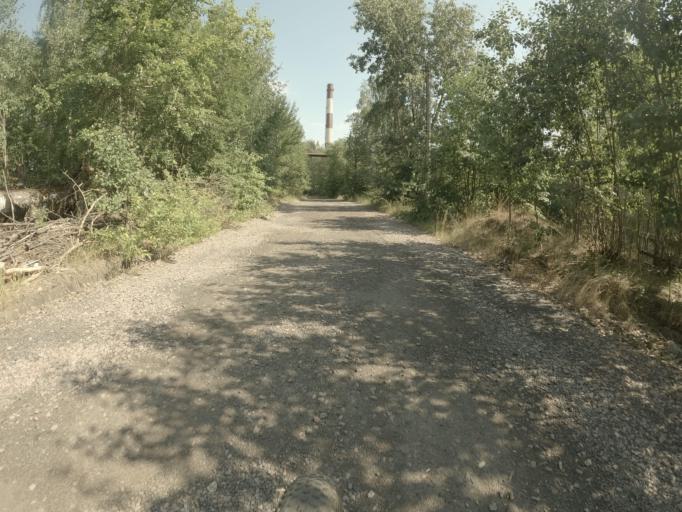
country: RU
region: St.-Petersburg
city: Centralniy
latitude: 59.9149
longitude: 30.4218
